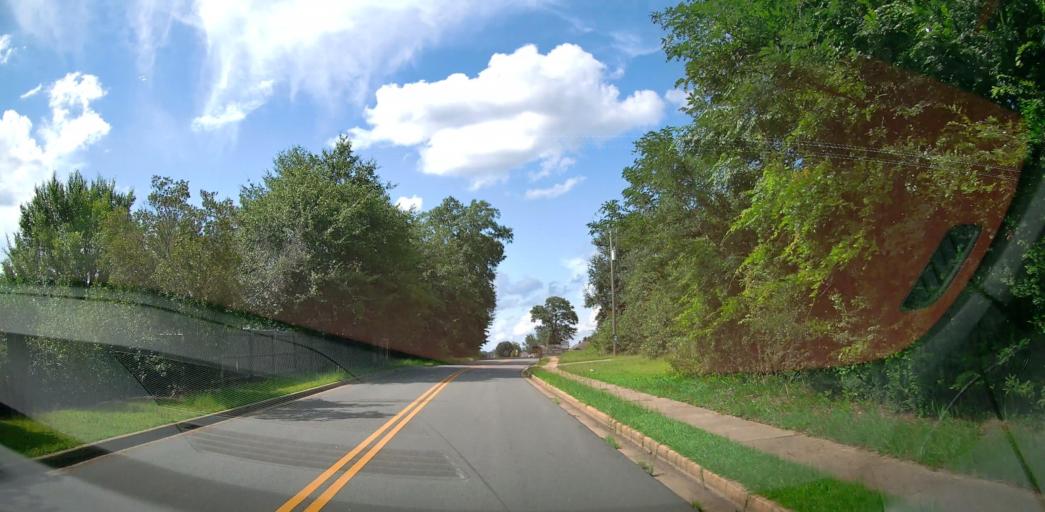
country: US
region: Georgia
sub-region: Houston County
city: Centerville
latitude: 32.5724
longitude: -83.7005
